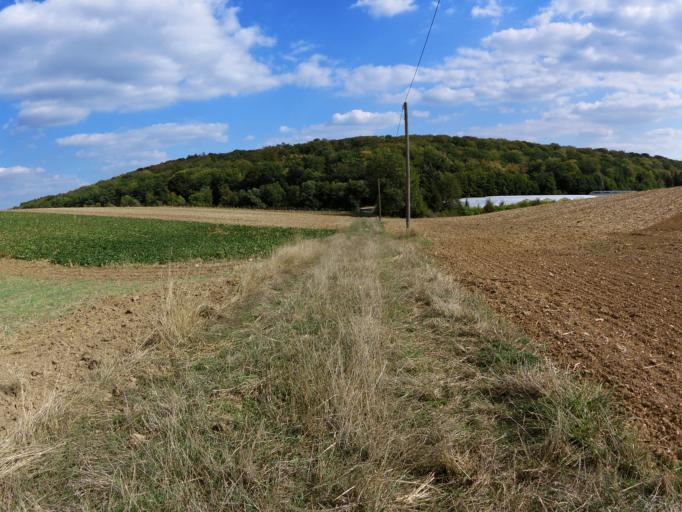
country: DE
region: Bavaria
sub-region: Regierungsbezirk Unterfranken
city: Hettstadt
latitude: 49.7903
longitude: 9.8012
